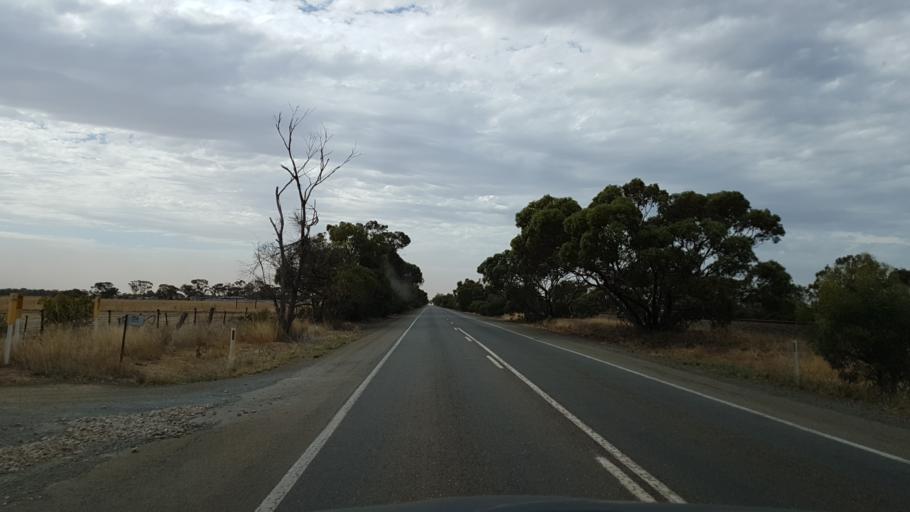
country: AU
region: South Australia
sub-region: Mallala
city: Mallala
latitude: -34.4310
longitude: 138.4956
